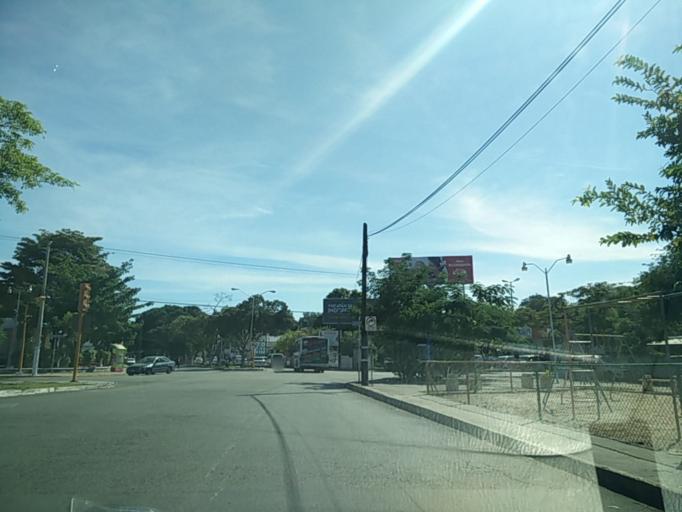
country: MX
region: Yucatan
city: Merida
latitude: 20.9962
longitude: -89.6012
